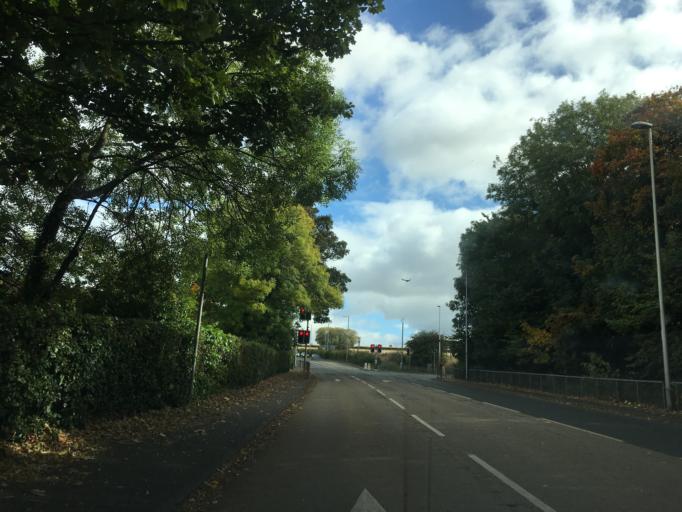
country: GB
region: Scotland
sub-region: Midlothian
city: Dalkeith
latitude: 55.8889
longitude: -3.0501
